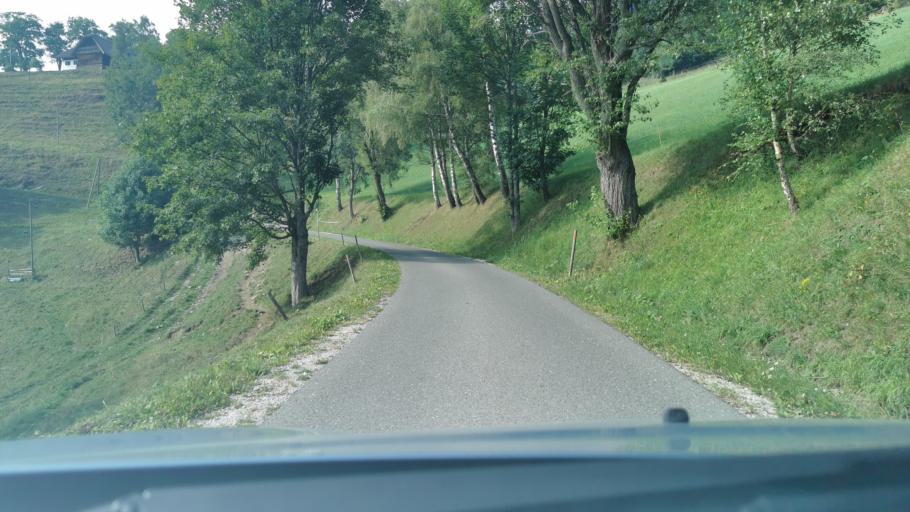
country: AT
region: Styria
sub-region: Politischer Bezirk Weiz
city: Fischbach
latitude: 47.3960
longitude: 15.6288
